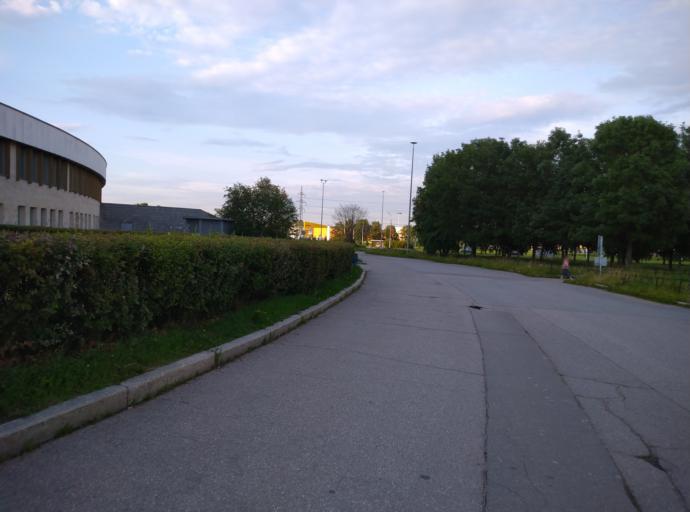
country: RU
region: St.-Petersburg
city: Kupchino
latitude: 59.8683
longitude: 30.3431
